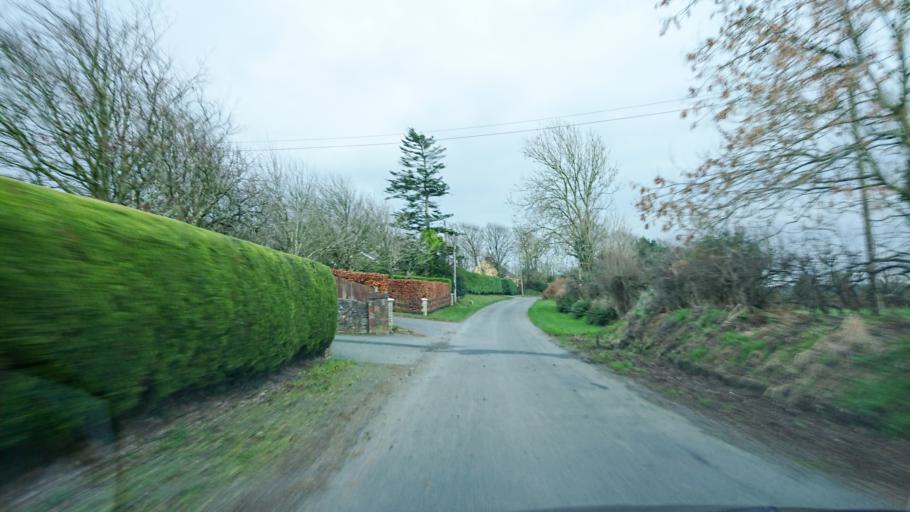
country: IE
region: Munster
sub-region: Waterford
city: Waterford
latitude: 52.2515
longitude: -7.0100
